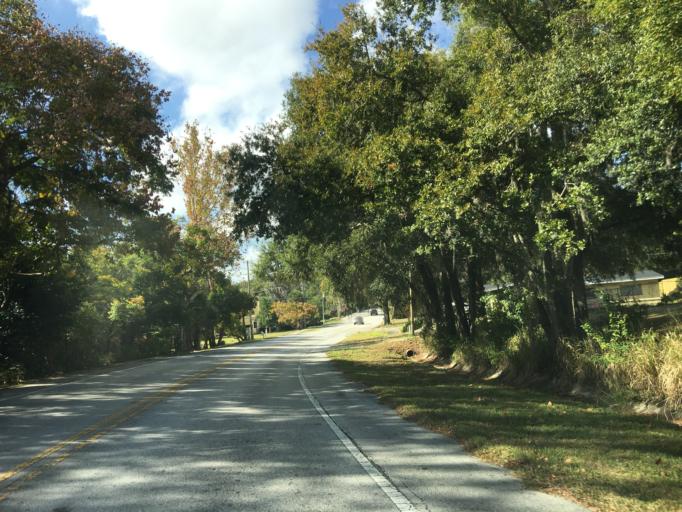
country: US
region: Florida
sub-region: Orange County
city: Eatonville
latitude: 28.6181
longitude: -81.3698
